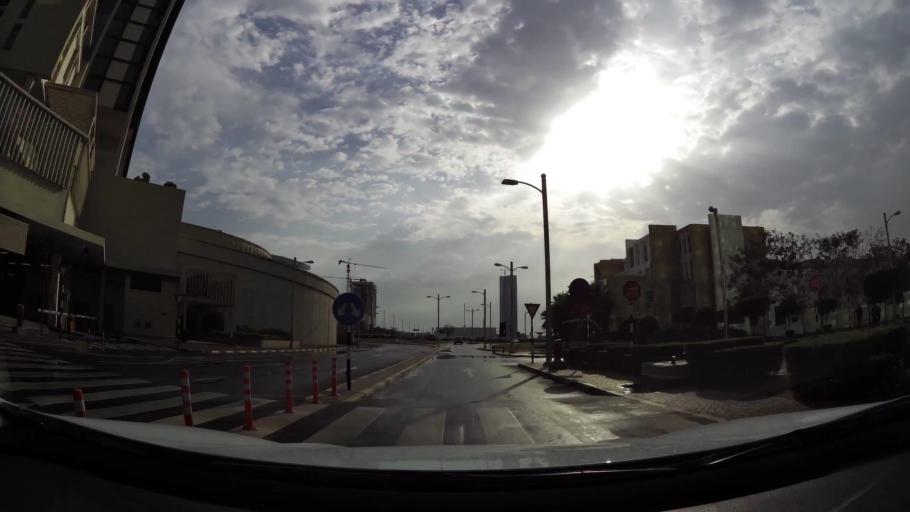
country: AE
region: Abu Dhabi
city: Abu Dhabi
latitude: 24.4902
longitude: 54.3949
